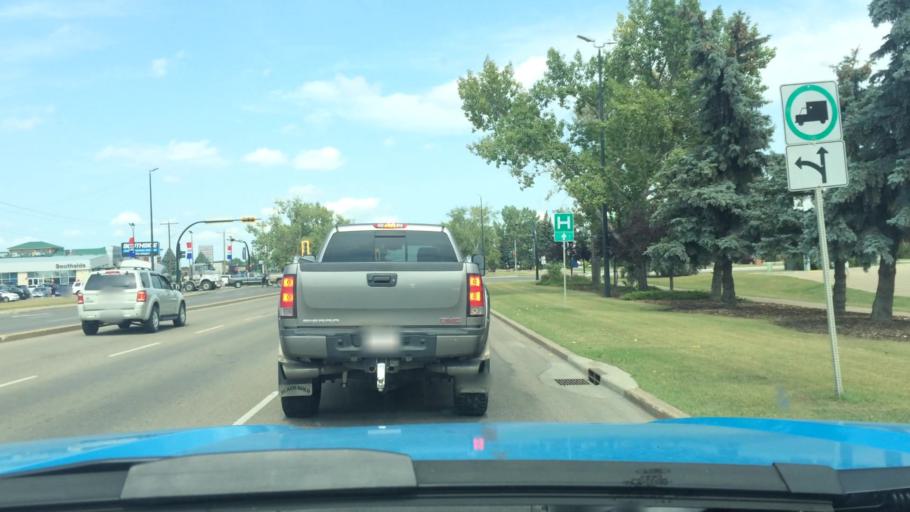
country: CA
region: Alberta
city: Red Deer
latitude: 52.2439
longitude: -113.8139
